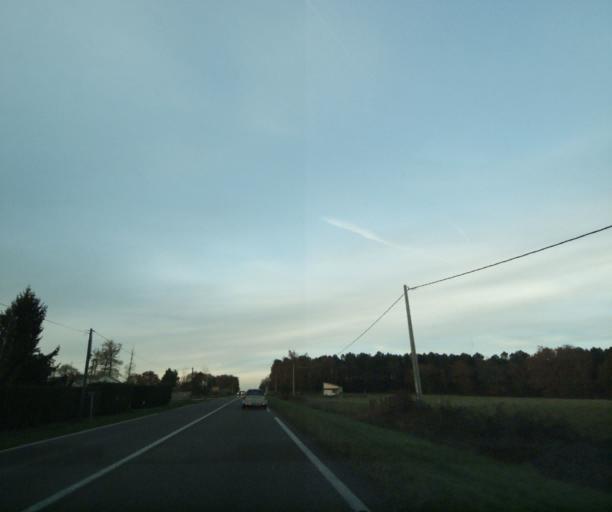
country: FR
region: Aquitaine
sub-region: Departement de la Gironde
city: Langon
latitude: 44.4926
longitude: -0.2350
